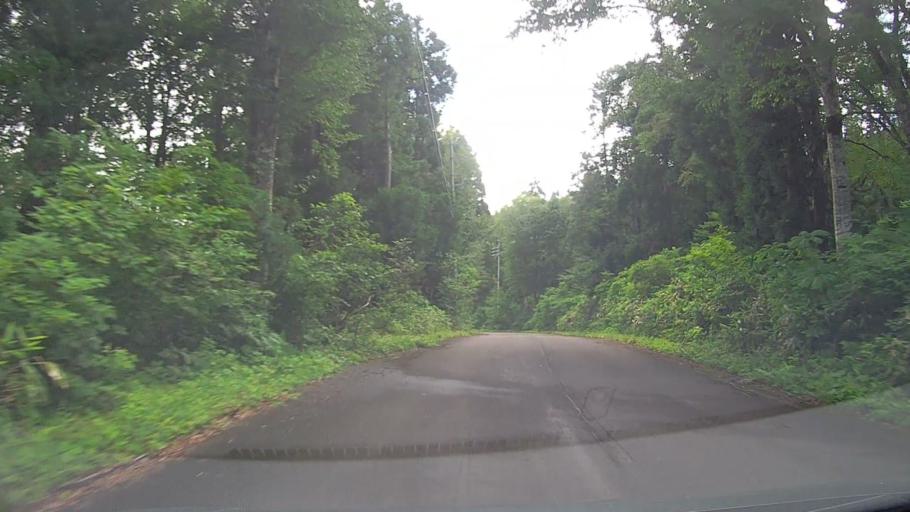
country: JP
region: Nagano
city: Iiyama
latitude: 36.9177
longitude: 138.4835
